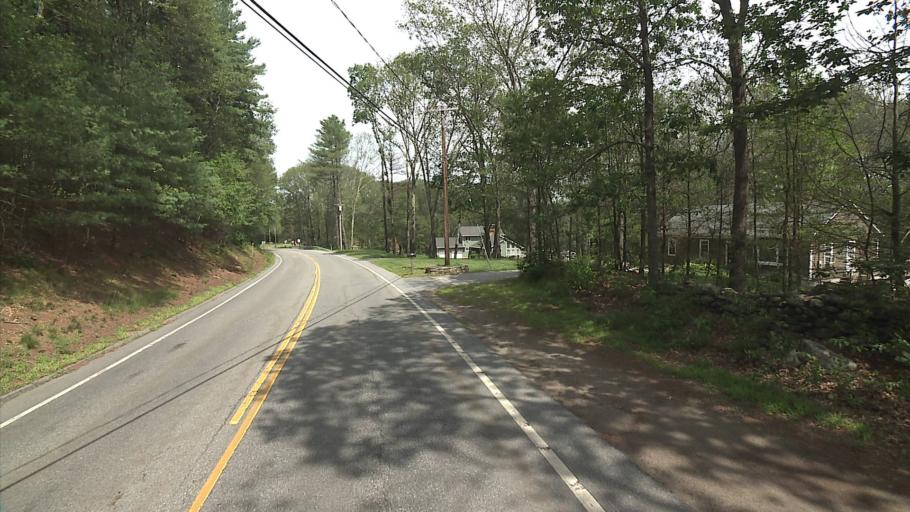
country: US
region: Connecticut
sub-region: Windham County
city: Putnam
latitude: 41.9067
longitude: -71.8668
